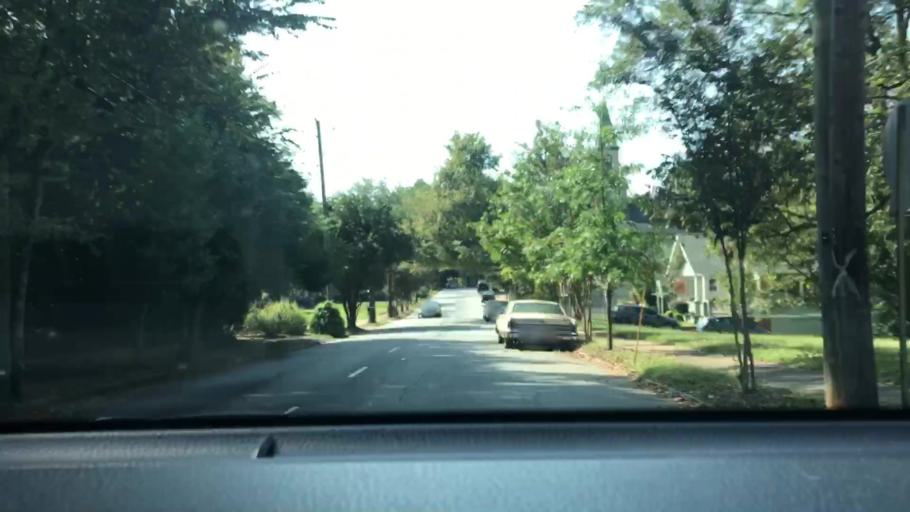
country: US
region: Georgia
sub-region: DeKalb County
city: Druid Hills
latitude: 33.7544
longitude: -84.3232
